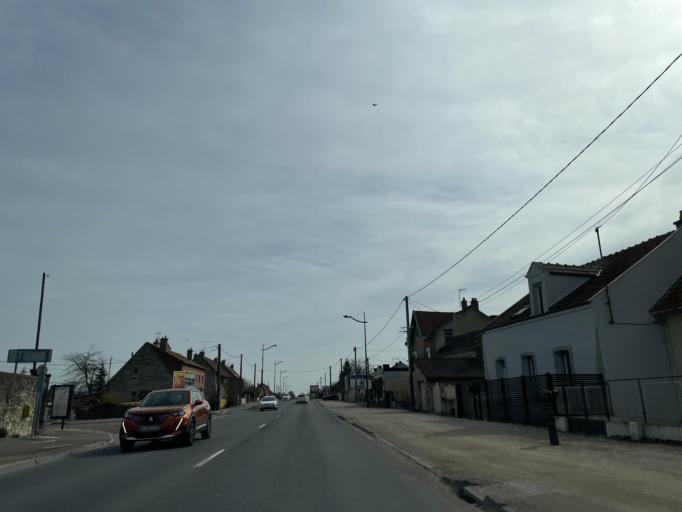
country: FR
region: Champagne-Ardenne
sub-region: Departement de l'Aube
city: Romilly-sur-Seine
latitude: 48.5081
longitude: 3.7398
